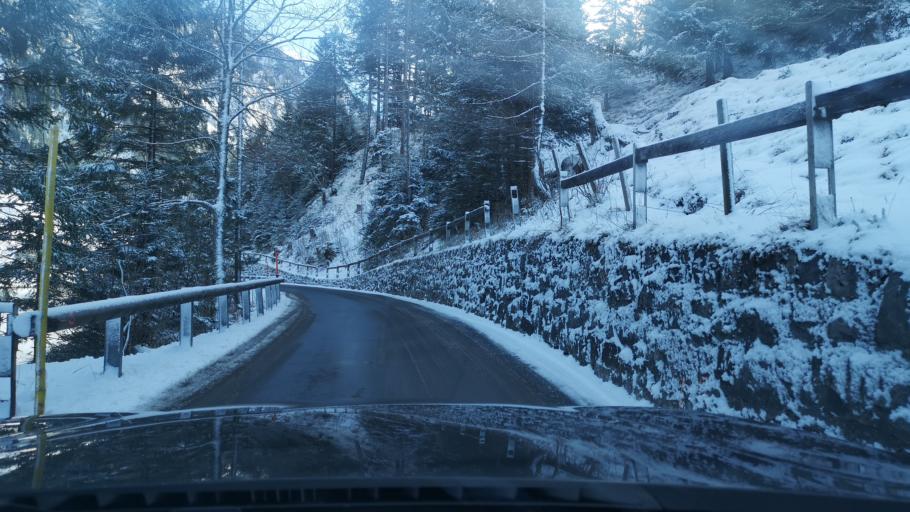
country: LI
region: Triesenberg
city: Triesenberg
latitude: 47.1109
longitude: 9.5732
